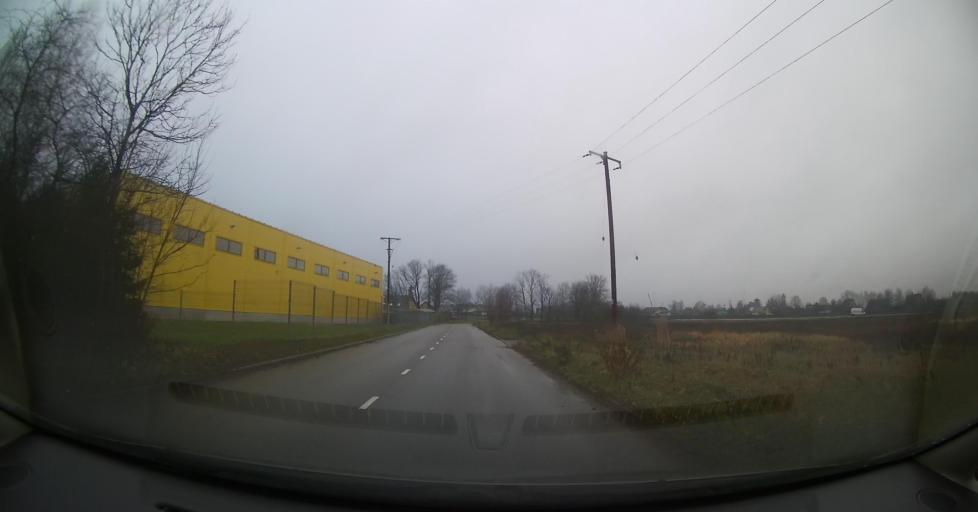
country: EE
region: Tartu
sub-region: Tartu linn
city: Tartu
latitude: 58.3715
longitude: 26.7949
